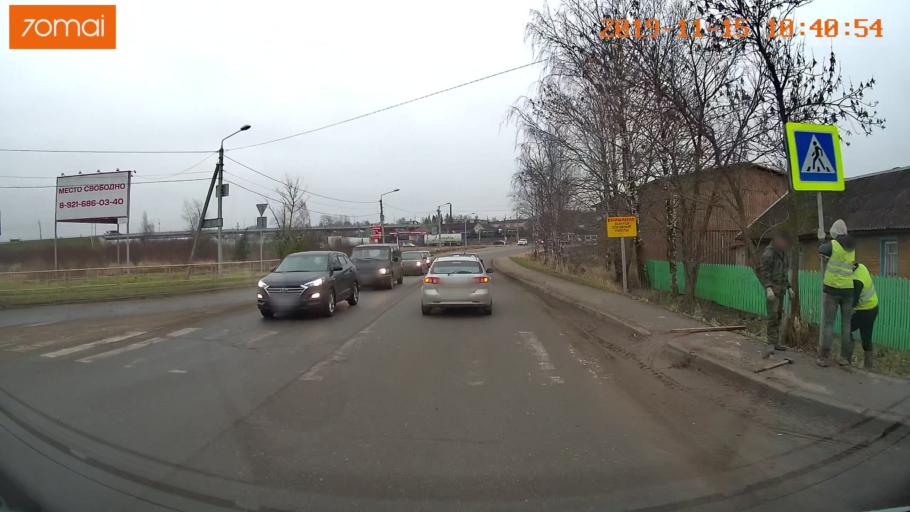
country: RU
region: Vologda
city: Sheksna
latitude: 59.2119
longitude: 38.5111
